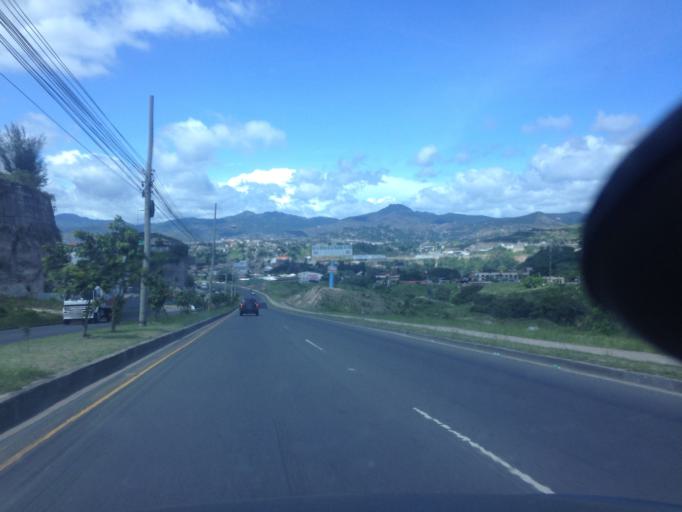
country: HN
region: Francisco Morazan
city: Yaguacire
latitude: 14.0453
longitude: -87.2179
